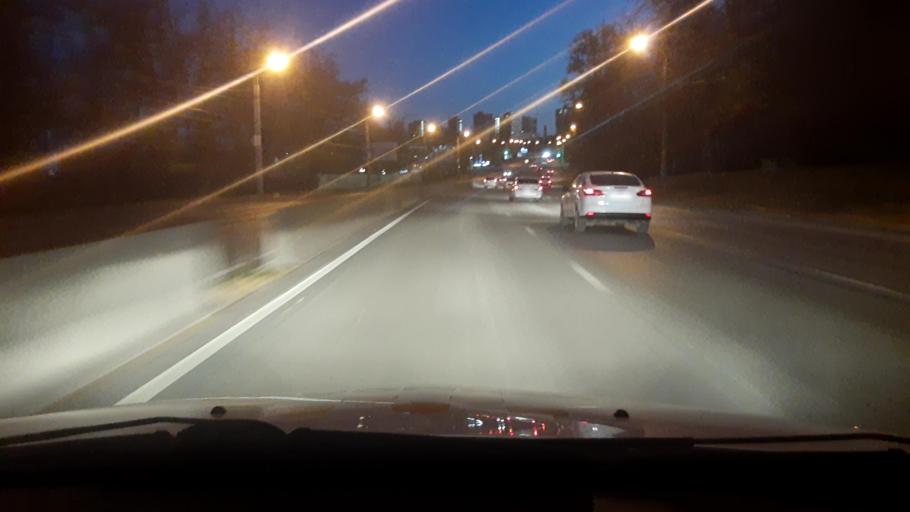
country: RU
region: Bashkortostan
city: Ufa
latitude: 54.7343
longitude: 56.0263
